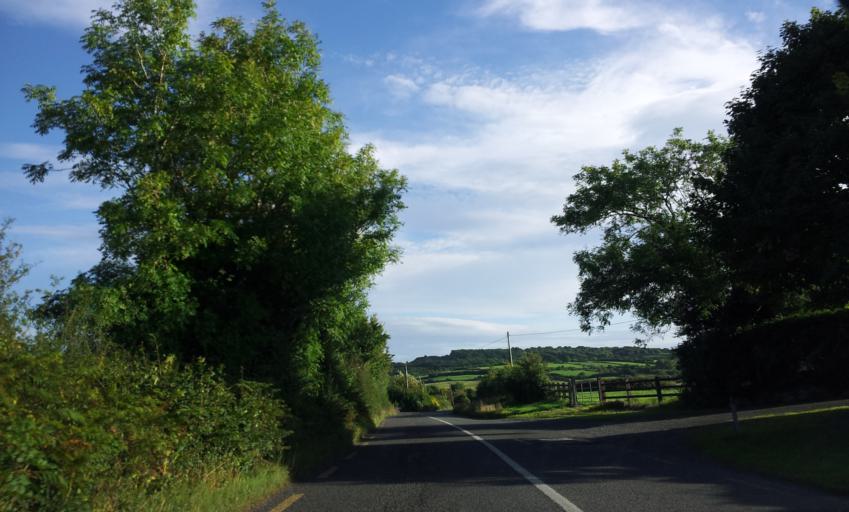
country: IE
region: Munster
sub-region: An Clar
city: Ennis
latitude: 52.9152
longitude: -9.0451
